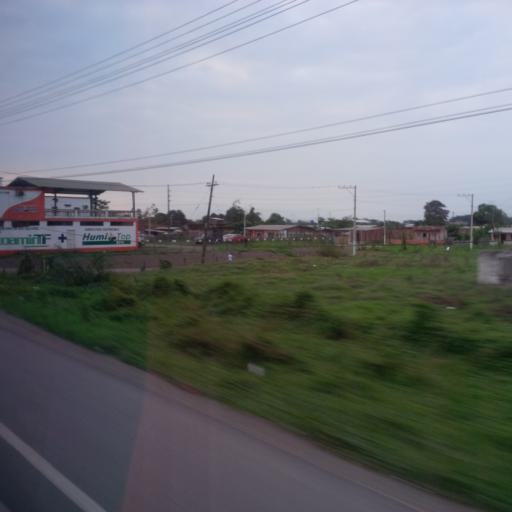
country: EC
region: Canar
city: La Troncal
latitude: -2.3273
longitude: -79.4106
